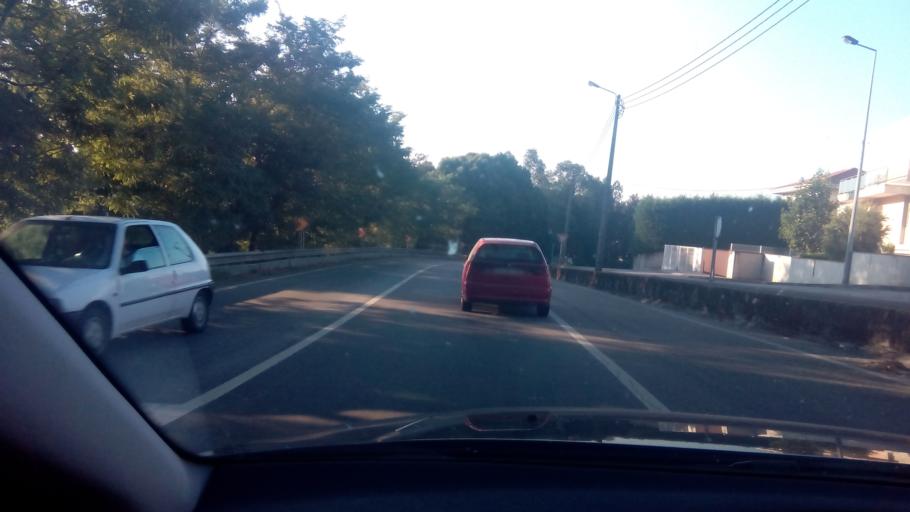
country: PT
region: Porto
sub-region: Paredes
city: Gandra
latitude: 41.1903
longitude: -8.4357
